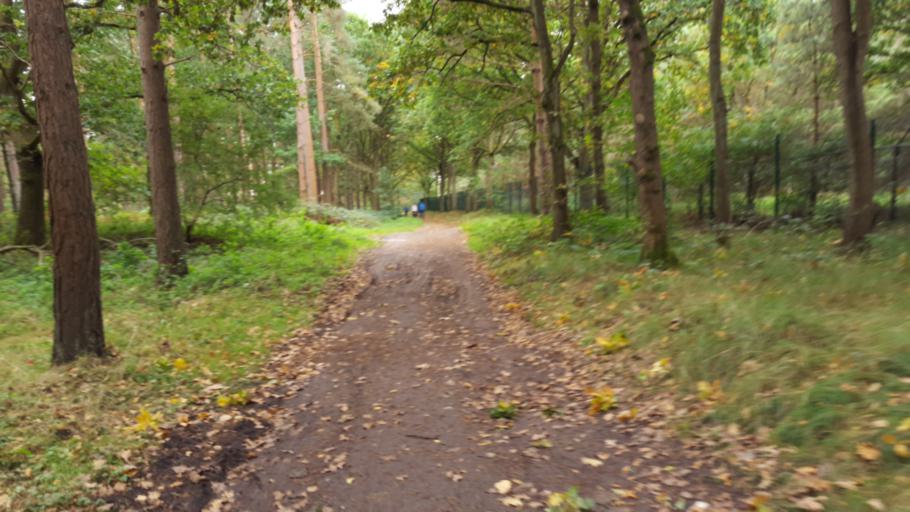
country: GB
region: England
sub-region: Norfolk
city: Weeting
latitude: 52.3940
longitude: 0.6317
